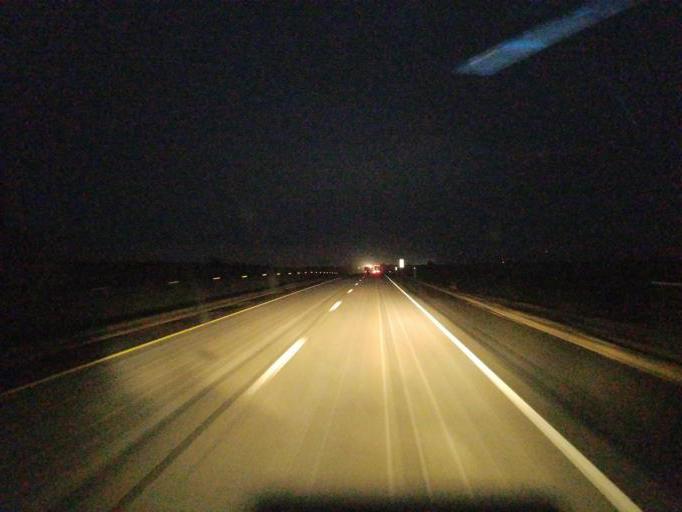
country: US
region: Iowa
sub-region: Guthrie County
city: Stuart
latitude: 41.4958
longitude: -94.4020
